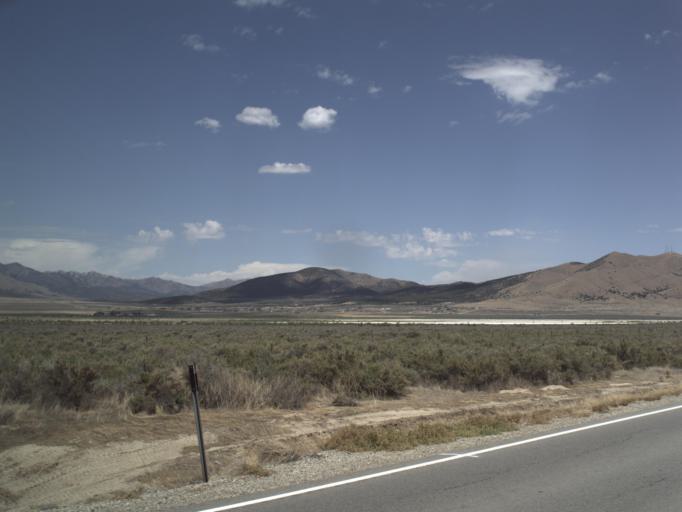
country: US
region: Utah
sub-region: Tooele County
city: Tooele
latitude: 40.3973
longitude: -112.3860
